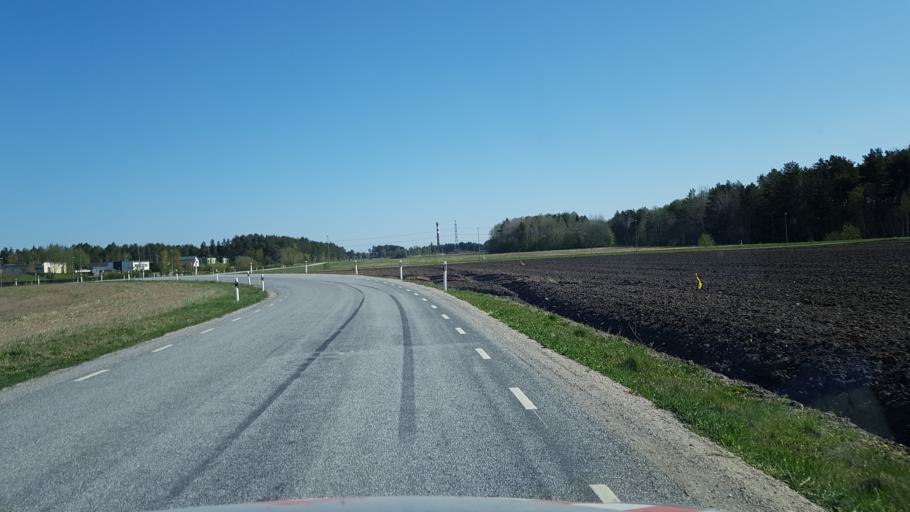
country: EE
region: Harju
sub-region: Saue vald
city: Laagri
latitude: 59.3397
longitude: 24.5869
